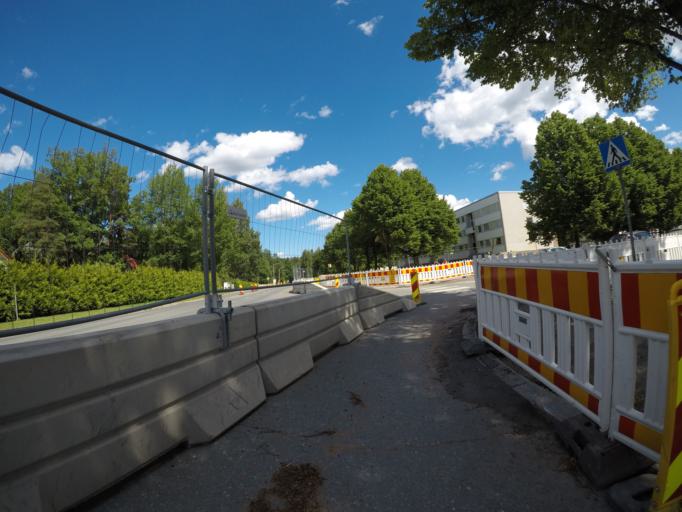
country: FI
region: Haeme
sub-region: Haemeenlinna
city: Haemeenlinna
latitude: 61.0076
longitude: 24.4423
